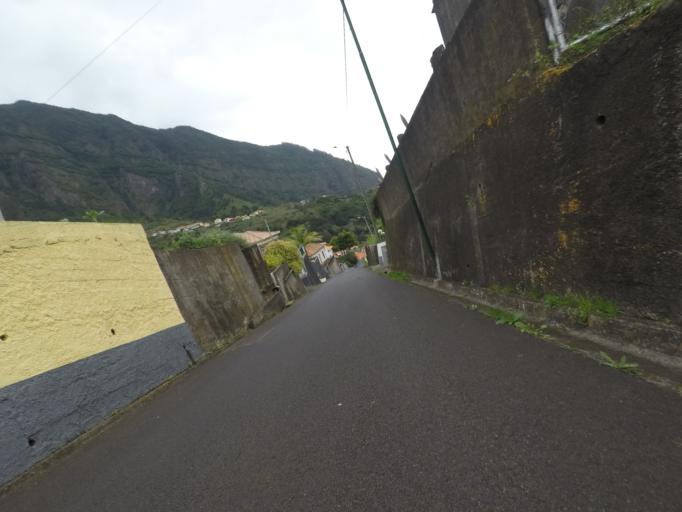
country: PT
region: Madeira
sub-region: Sao Vicente
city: Sao Vicente
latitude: 32.7924
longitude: -17.0401
